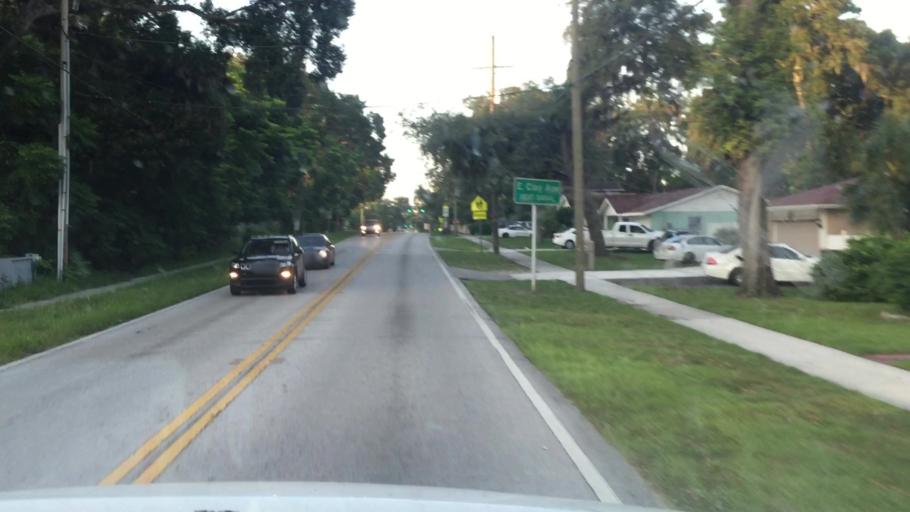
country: US
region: Florida
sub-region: Hillsborough County
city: Brandon
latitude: 27.9468
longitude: -82.2777
